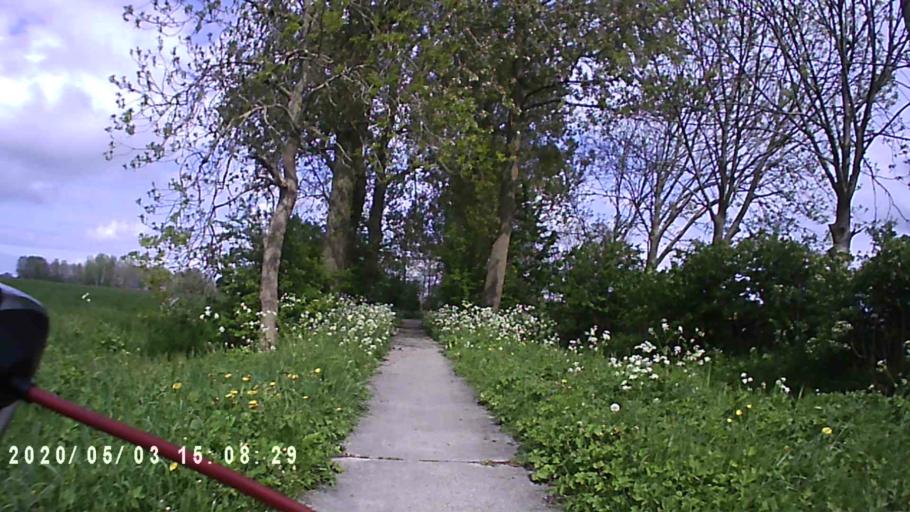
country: NL
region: Groningen
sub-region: Gemeente Zuidhorn
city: Oldehove
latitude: 53.3765
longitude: 6.4428
